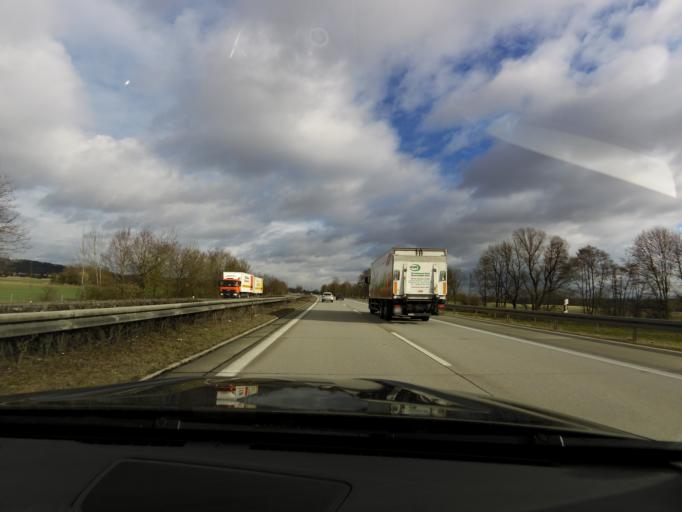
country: DE
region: Bavaria
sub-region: Lower Bavaria
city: Eching
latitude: 48.5164
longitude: 12.0592
